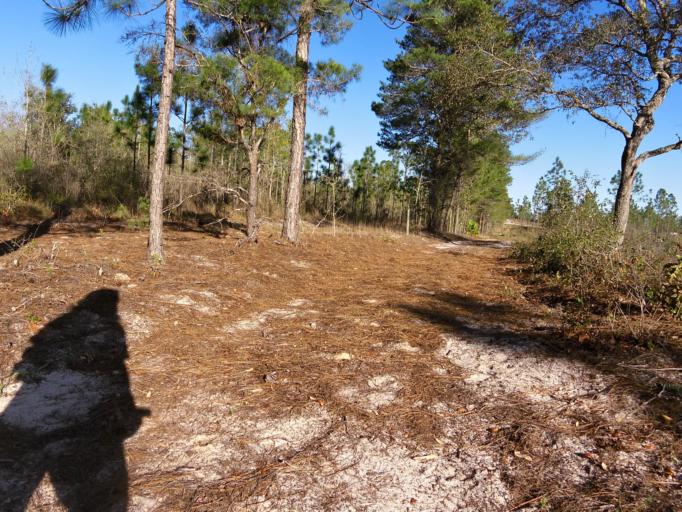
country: US
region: Florida
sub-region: Clay County
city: Keystone Heights
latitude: 29.8382
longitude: -81.9823
